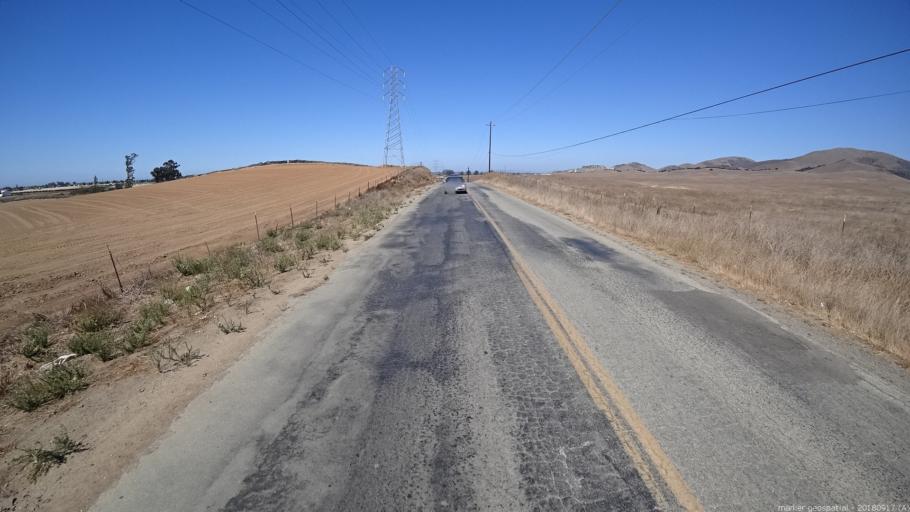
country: US
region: California
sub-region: Monterey County
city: Salinas
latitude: 36.7080
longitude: -121.5827
